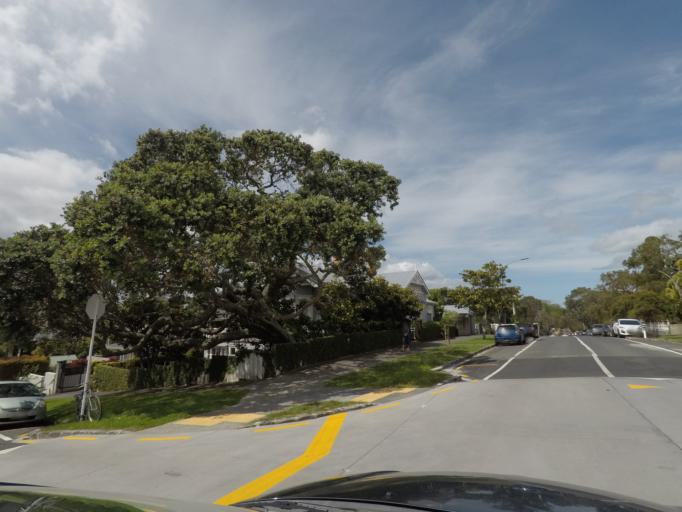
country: NZ
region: Auckland
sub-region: Auckland
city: Auckland
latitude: -36.8413
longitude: 174.7371
